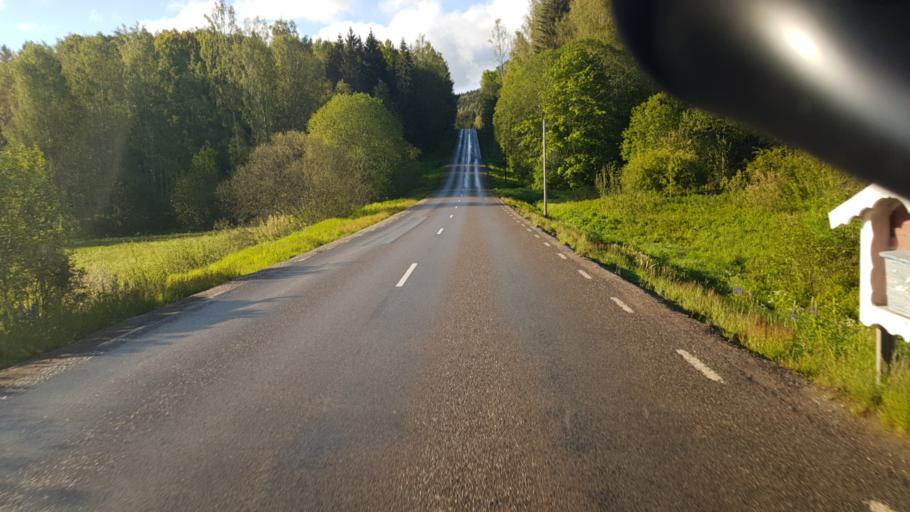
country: SE
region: Vaermland
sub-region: Eda Kommun
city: Amotfors
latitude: 59.6680
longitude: 12.4219
